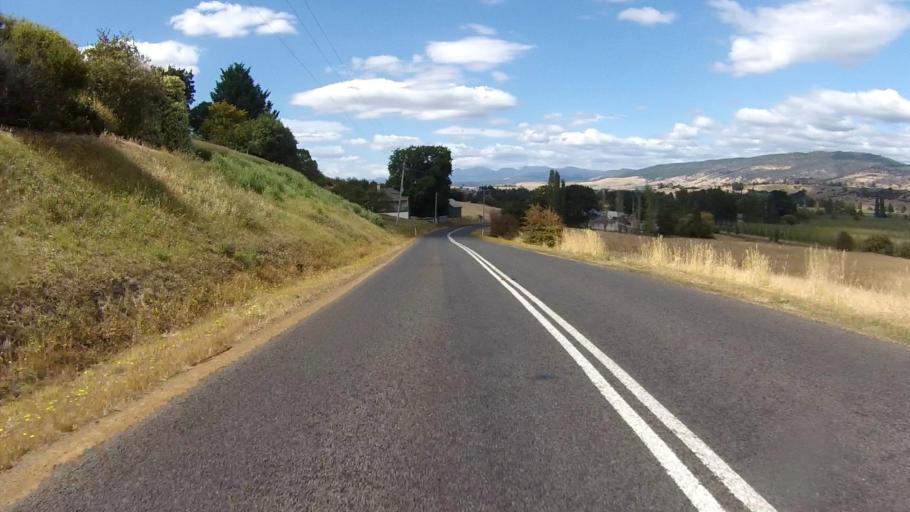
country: AU
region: Tasmania
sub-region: Derwent Valley
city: New Norfolk
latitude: -42.6920
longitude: 146.8844
